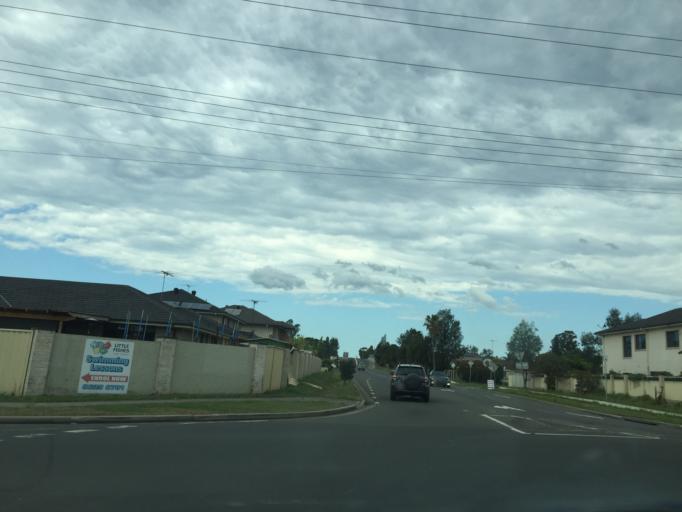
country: AU
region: New South Wales
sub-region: Blacktown
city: Glendenning
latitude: -33.7443
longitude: 150.8427
